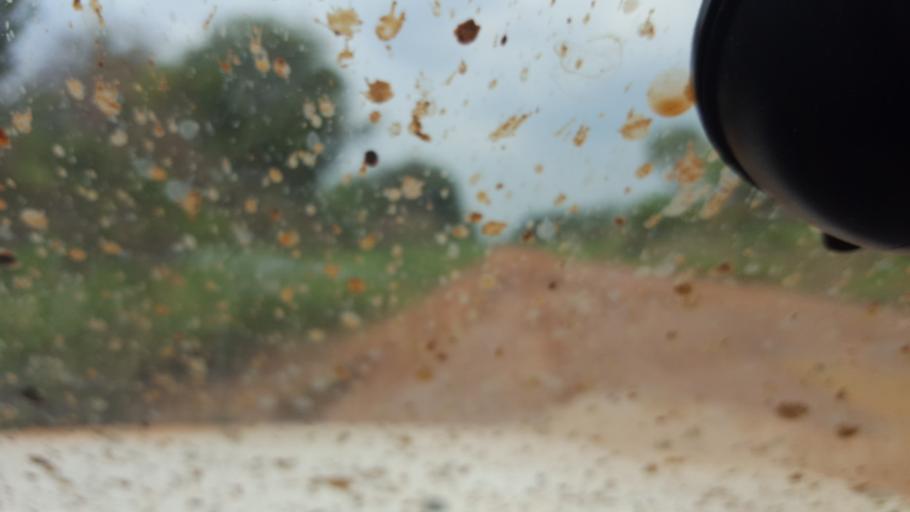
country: CD
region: Bandundu
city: Bandundu
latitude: -3.7592
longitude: 17.1533
